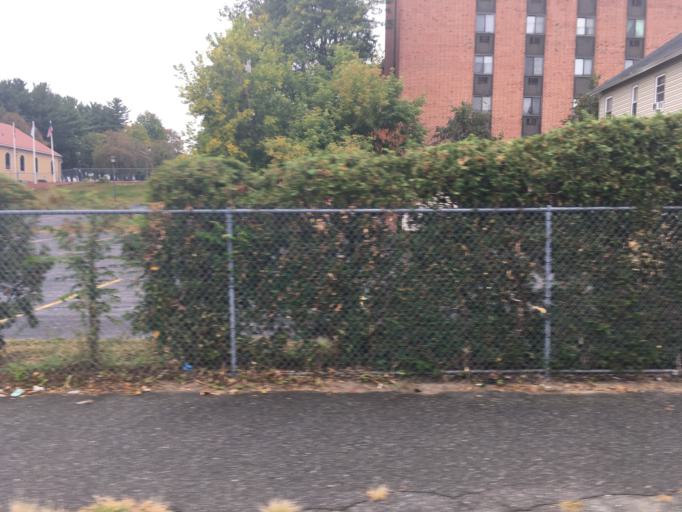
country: US
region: Massachusetts
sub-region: Middlesex County
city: Lowell
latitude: 42.6487
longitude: -71.3221
